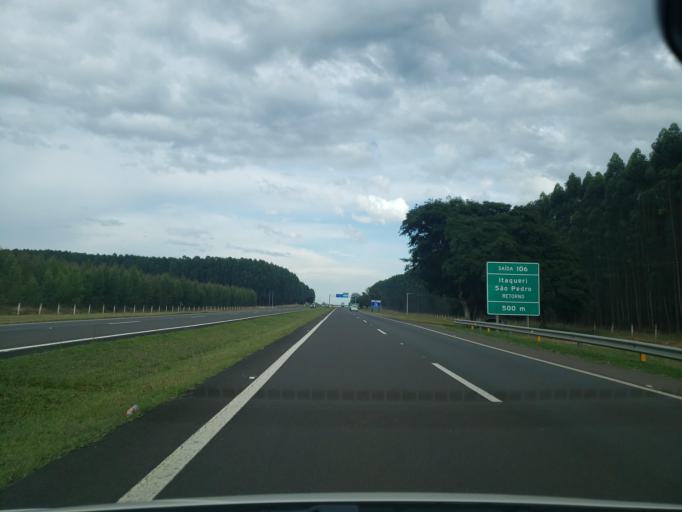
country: BR
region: Sao Paulo
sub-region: Itirapina
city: Itirapina
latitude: -22.2610
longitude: -47.8852
